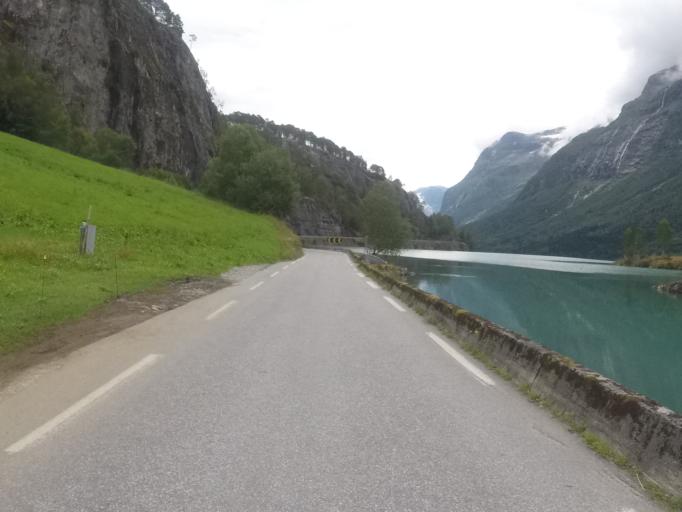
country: NO
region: Sogn og Fjordane
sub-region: Stryn
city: Stryn
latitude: 61.8597
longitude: 6.8905
